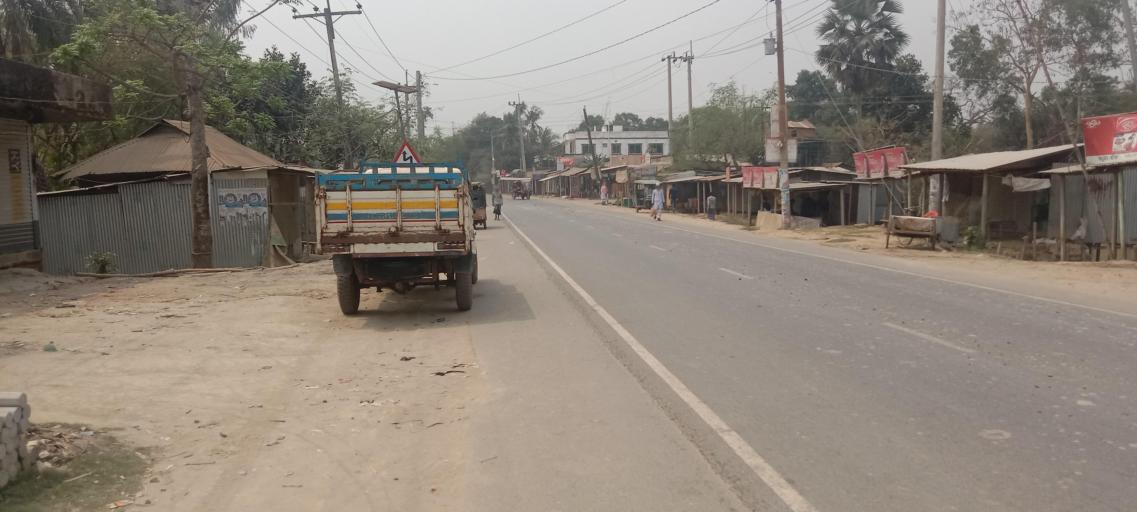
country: BD
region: Dhaka
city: Gafargaon
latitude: 24.4146
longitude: 90.4350
